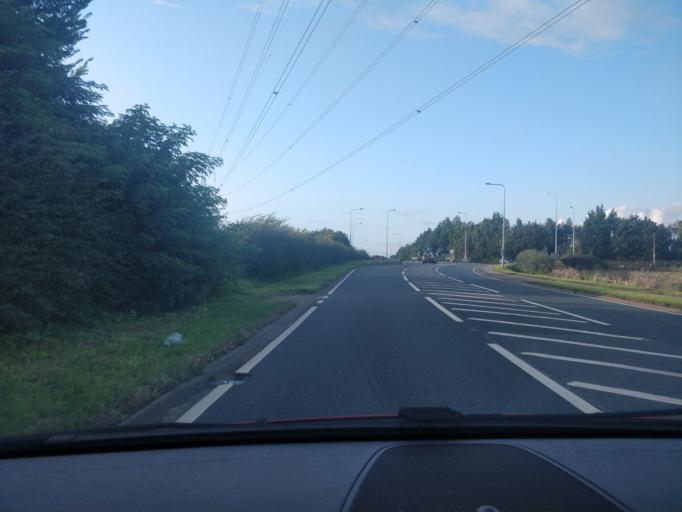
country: GB
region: England
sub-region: Lancashire
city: Tarleton
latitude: 53.6853
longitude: -2.8163
